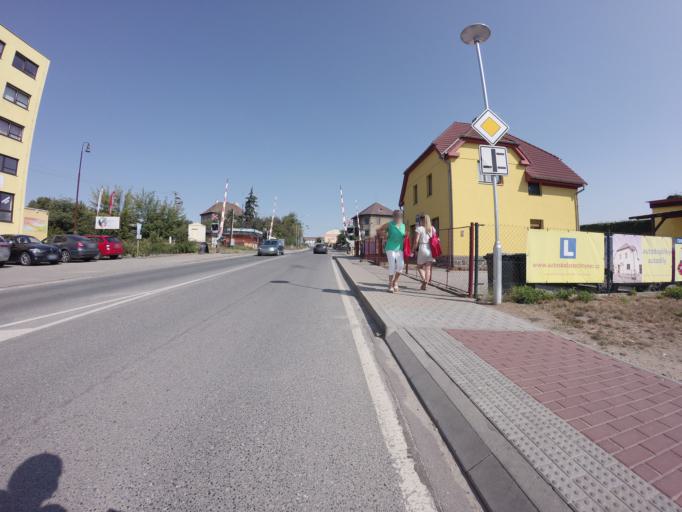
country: CZ
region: Central Bohemia
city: Tynec nad Sazavou
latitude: 49.8330
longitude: 14.5899
